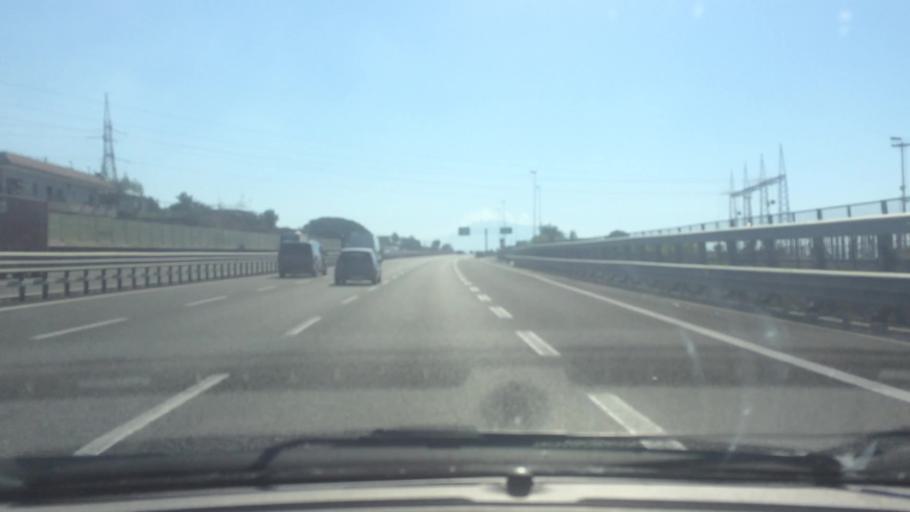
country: IT
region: Campania
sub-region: Provincia di Napoli
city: Ercolano
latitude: 40.8096
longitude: 14.3624
